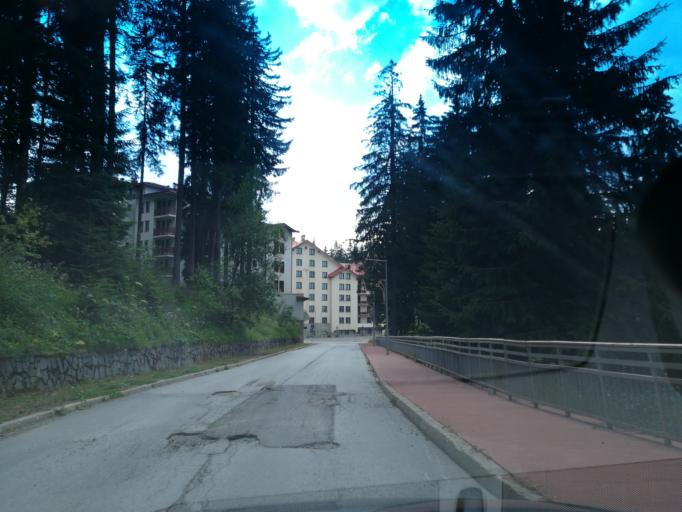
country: BG
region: Smolyan
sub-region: Obshtina Smolyan
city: Smolyan
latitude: 41.6555
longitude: 24.6927
